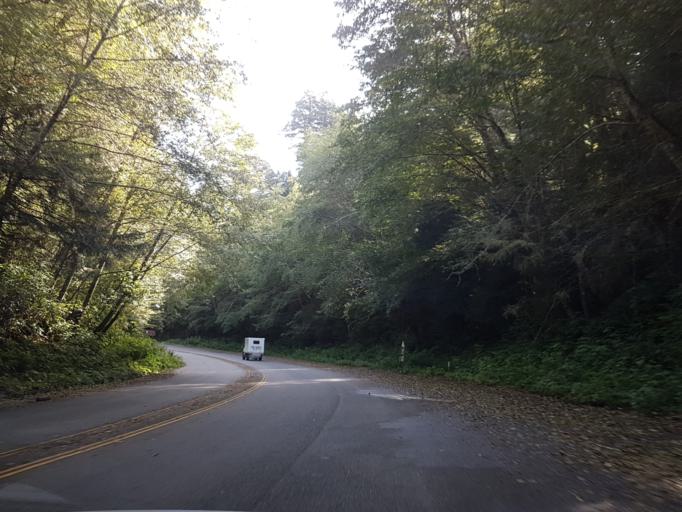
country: US
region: California
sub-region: Del Norte County
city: Bertsch-Oceanview
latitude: 41.4595
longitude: -124.0476
